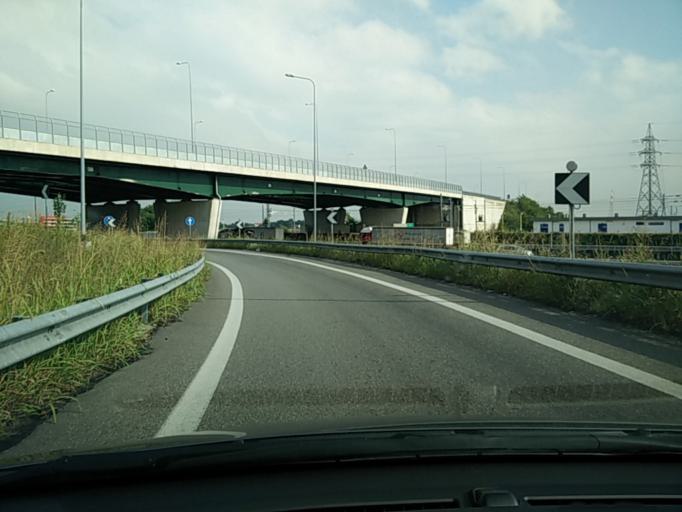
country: IT
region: Lombardy
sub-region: Citta metropolitana di Milano
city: Mesero
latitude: 45.4848
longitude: 8.8480
